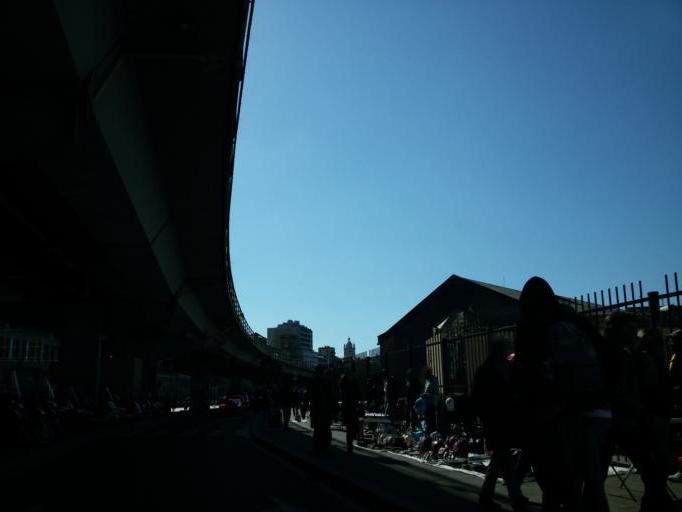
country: IT
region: Liguria
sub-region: Provincia di Genova
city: San Teodoro
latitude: 44.4132
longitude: 8.9261
